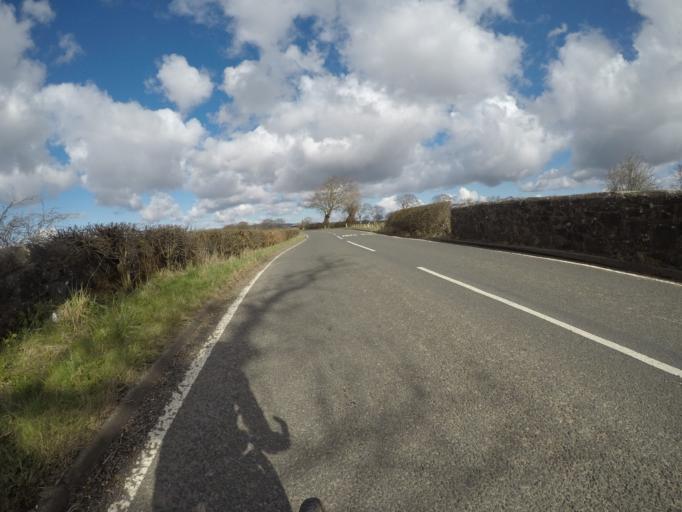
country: GB
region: Scotland
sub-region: North Ayrshire
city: Beith
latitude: 55.7358
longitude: -4.6174
